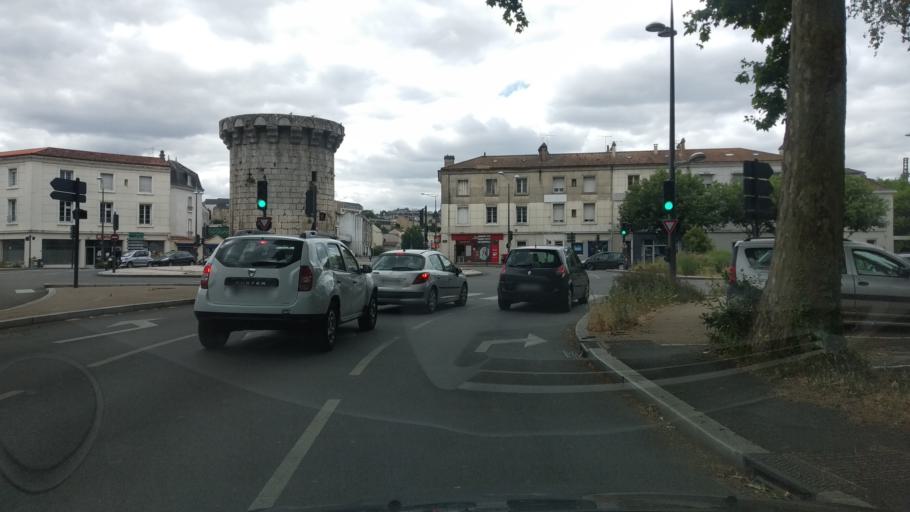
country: FR
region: Poitou-Charentes
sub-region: Departement de la Vienne
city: Poitiers
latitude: 46.5909
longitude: 0.3402
